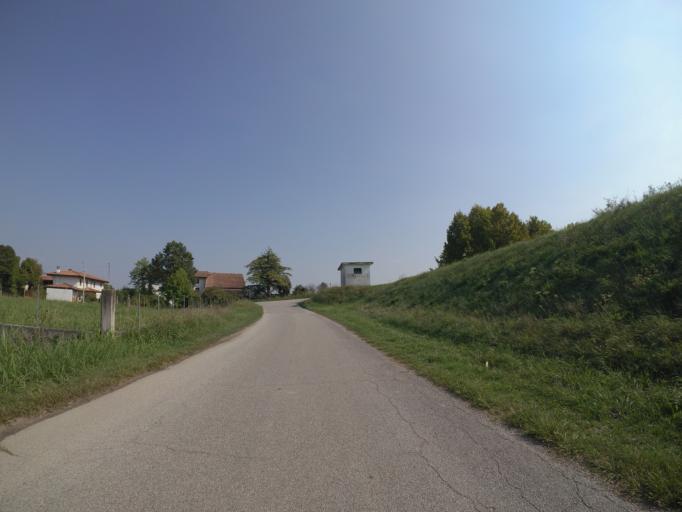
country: IT
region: Friuli Venezia Giulia
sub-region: Provincia di Udine
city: Varmo
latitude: 45.8900
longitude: 12.9590
